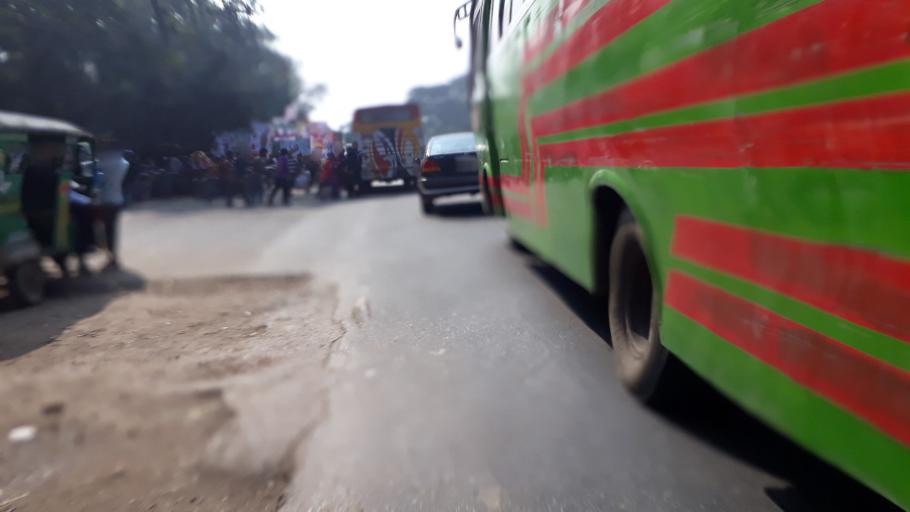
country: BD
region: Dhaka
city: Tungi
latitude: 23.8726
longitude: 90.2733
